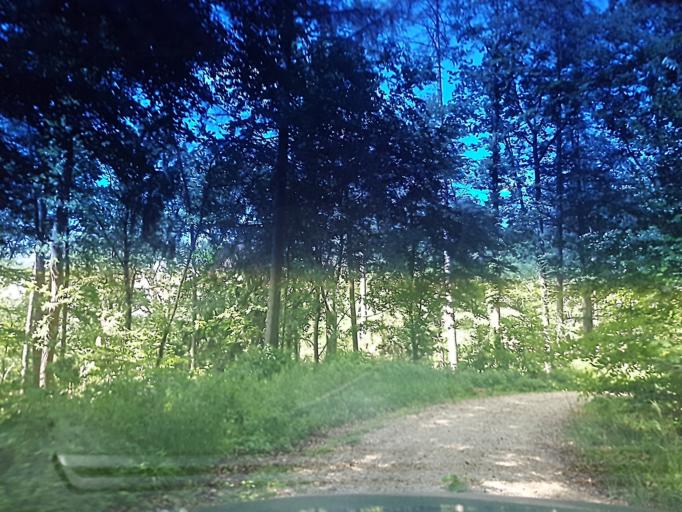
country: DE
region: Bavaria
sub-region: Upper Franconia
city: Litzendorf
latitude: 49.9372
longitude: 11.0257
